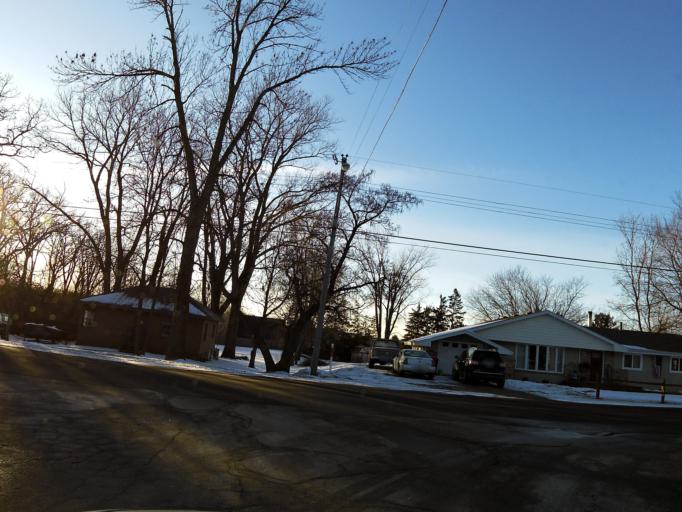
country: US
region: Minnesota
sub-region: Washington County
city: Cottage Grove
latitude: 44.8373
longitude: -92.8826
